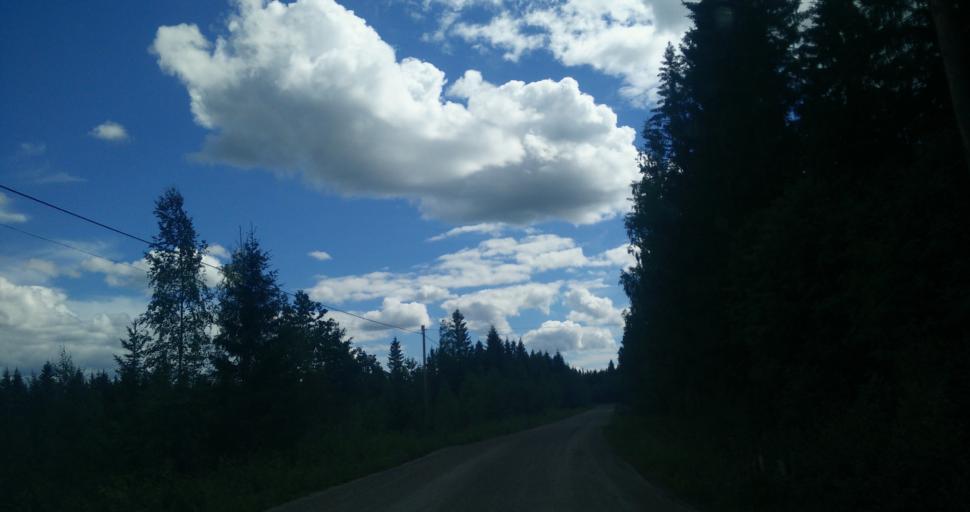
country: SE
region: Gaevleborg
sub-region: Nordanstigs Kommun
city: Bergsjoe
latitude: 62.0626
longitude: 16.7805
